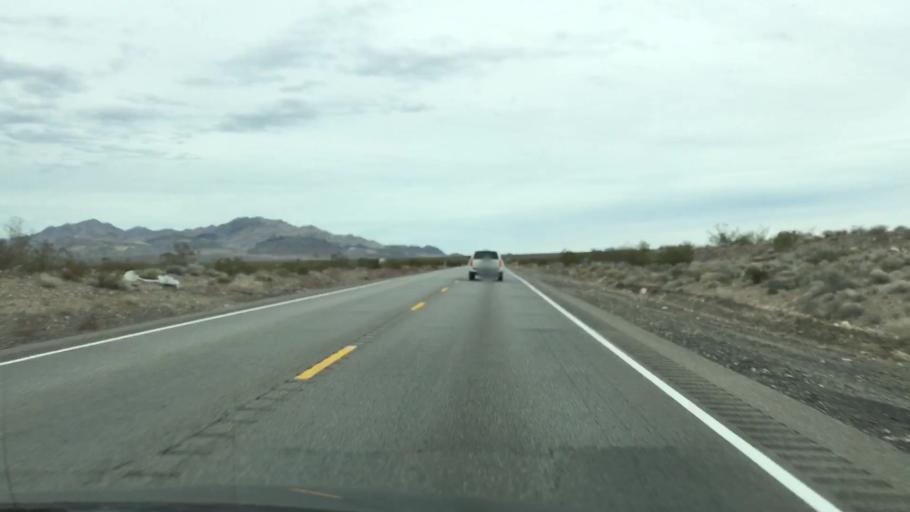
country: US
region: Nevada
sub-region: Nye County
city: Pahrump
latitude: 36.5891
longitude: -116.0475
